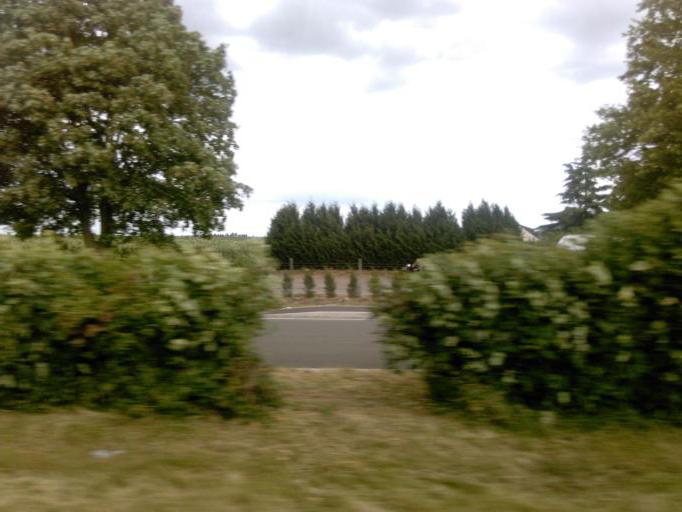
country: FR
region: Ile-de-France
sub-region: Departement du Val-d'Oise
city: Osny
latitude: 49.0786
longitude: 2.0728
